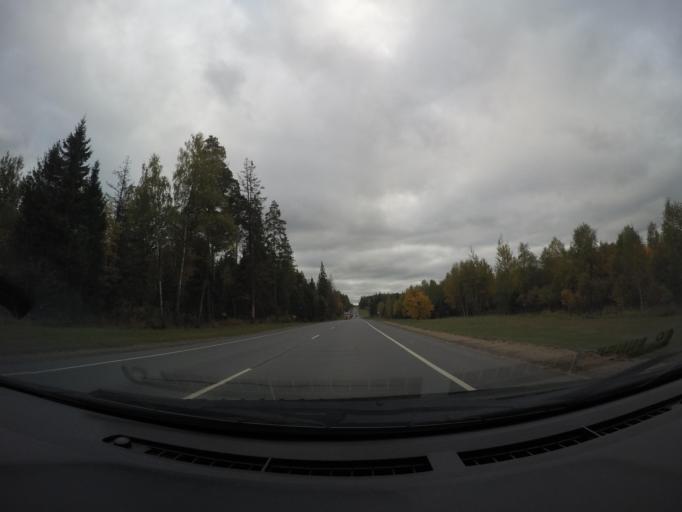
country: RU
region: Moskovskaya
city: Dorokhovo
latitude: 55.6180
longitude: 36.3462
